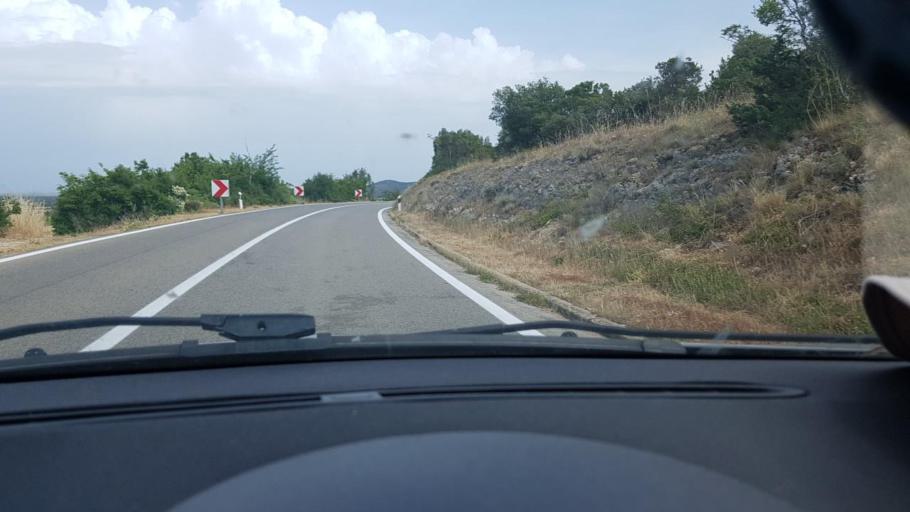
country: HR
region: Sibensko-Kniniska
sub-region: Grad Sibenik
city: Pirovac
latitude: 43.8655
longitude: 15.7419
